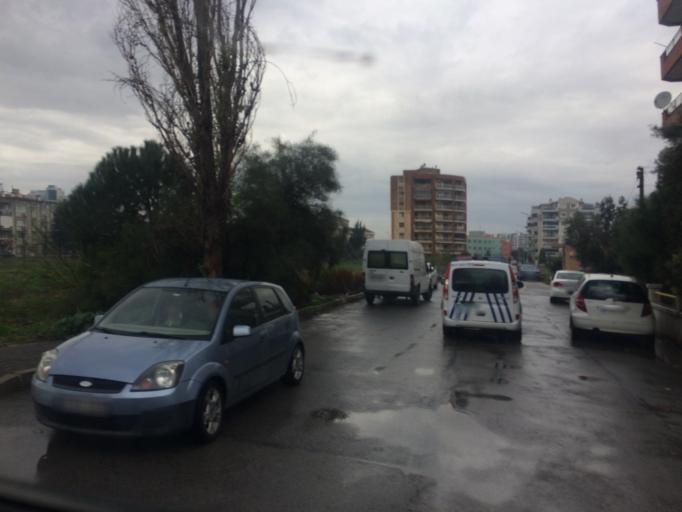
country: TR
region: Izmir
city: Karsiyaka
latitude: 38.4904
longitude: 27.0559
